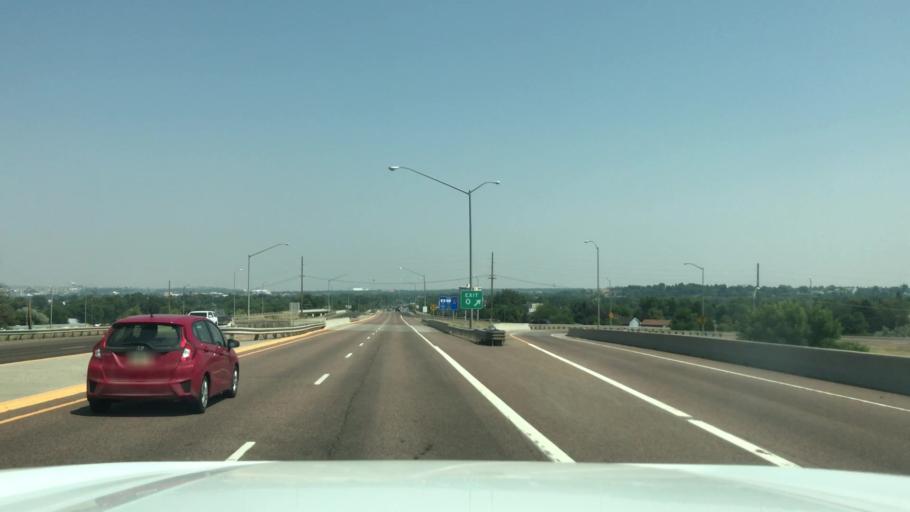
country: US
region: Montana
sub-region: Cascade County
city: Great Falls
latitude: 47.4864
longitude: -111.3394
